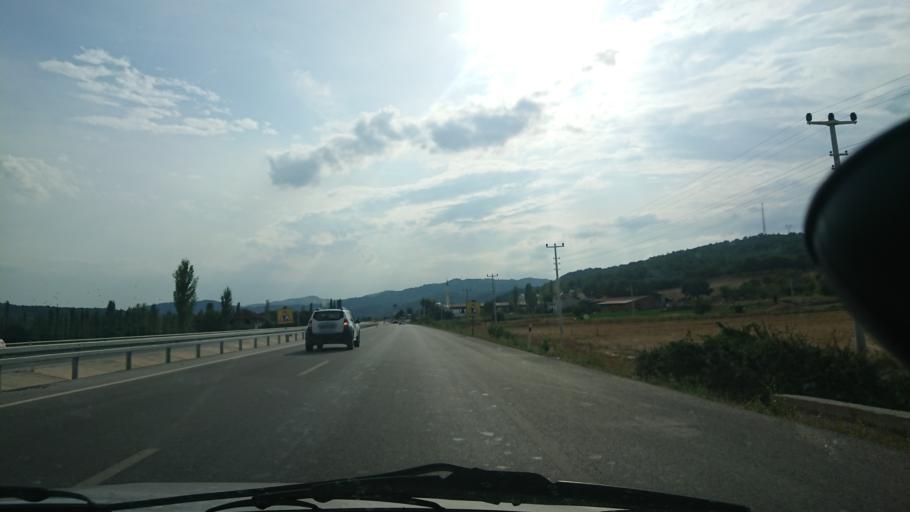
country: TR
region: Kuetahya
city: Gediz
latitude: 38.9399
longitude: 29.3206
